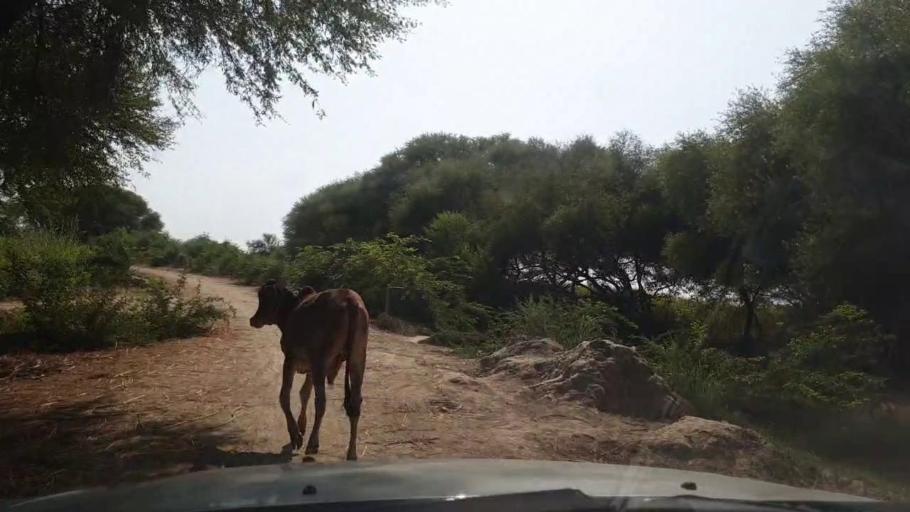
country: PK
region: Sindh
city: Bulri
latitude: 24.8714
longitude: 68.3105
